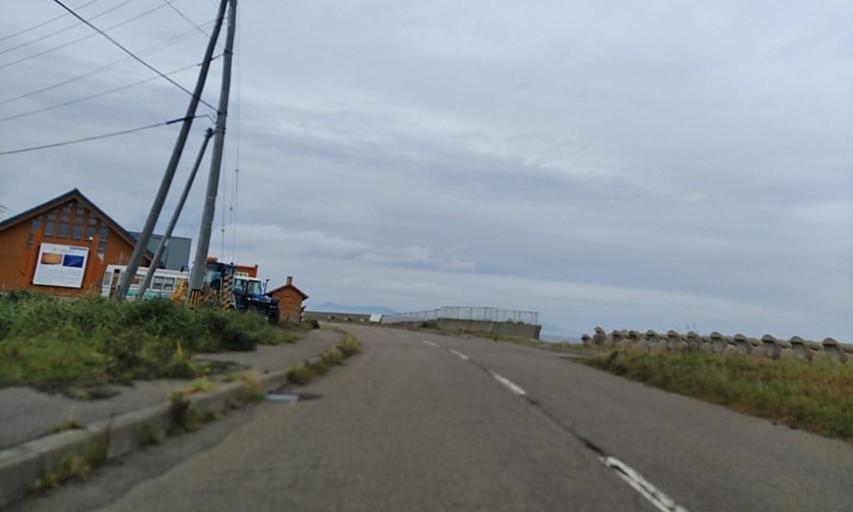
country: JP
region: Hokkaido
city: Shibetsu
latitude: 43.5898
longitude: 145.3358
